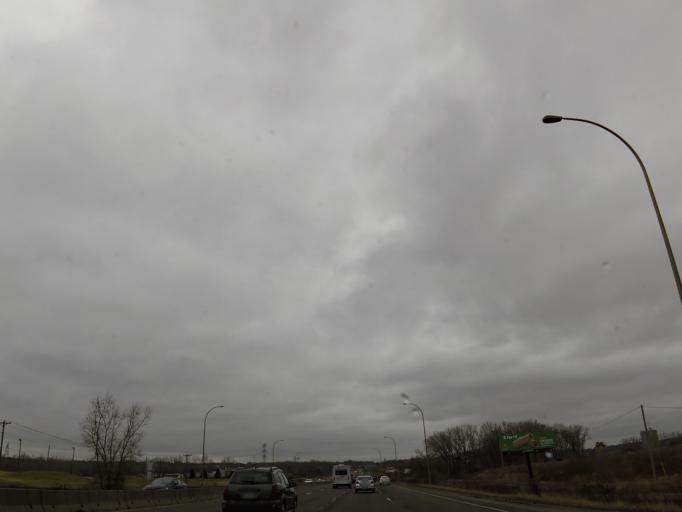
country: US
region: Minnesota
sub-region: Dakota County
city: Burnsville
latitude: 44.7901
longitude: -93.2890
